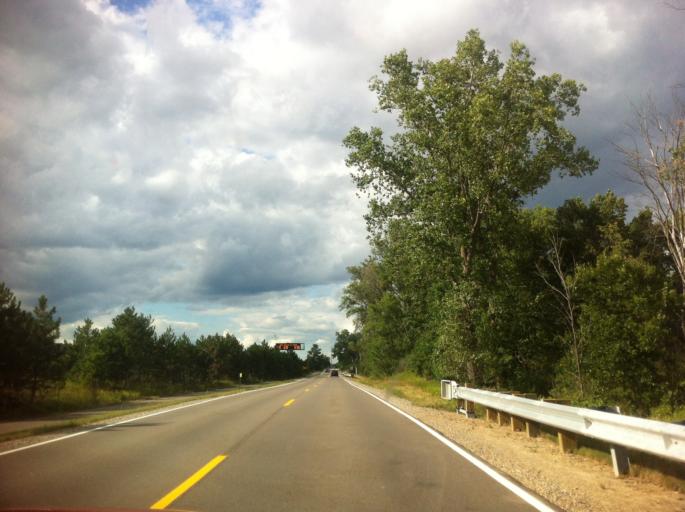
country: US
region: Michigan
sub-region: Livingston County
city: Brighton
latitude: 42.4904
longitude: -83.7569
